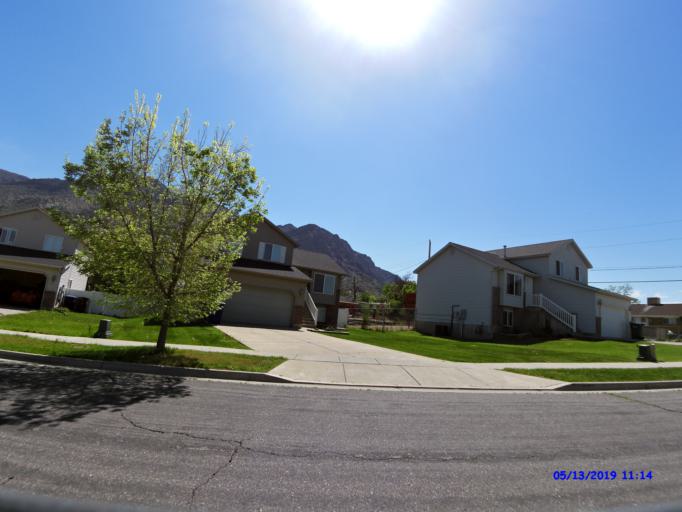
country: US
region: Utah
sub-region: Weber County
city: Harrisville
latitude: 41.2780
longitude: -111.9638
